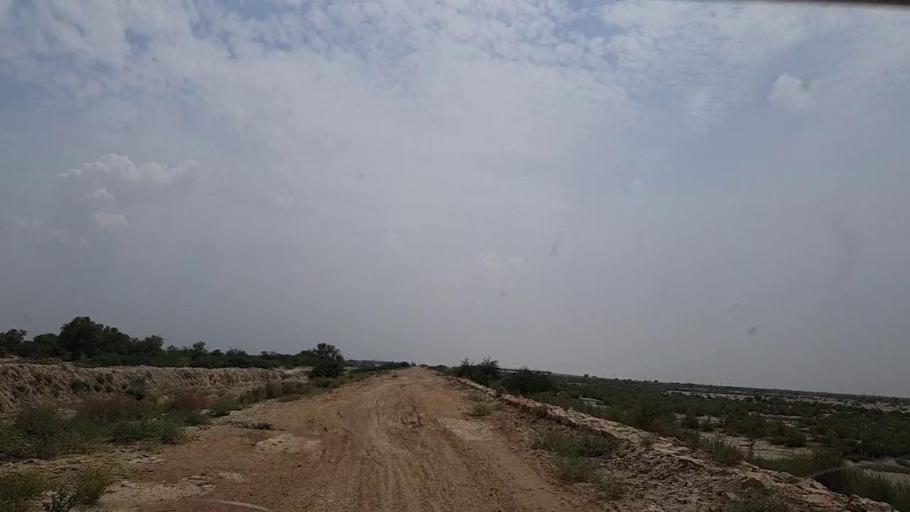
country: PK
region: Sindh
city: Phulji
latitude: 26.8276
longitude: 67.6157
